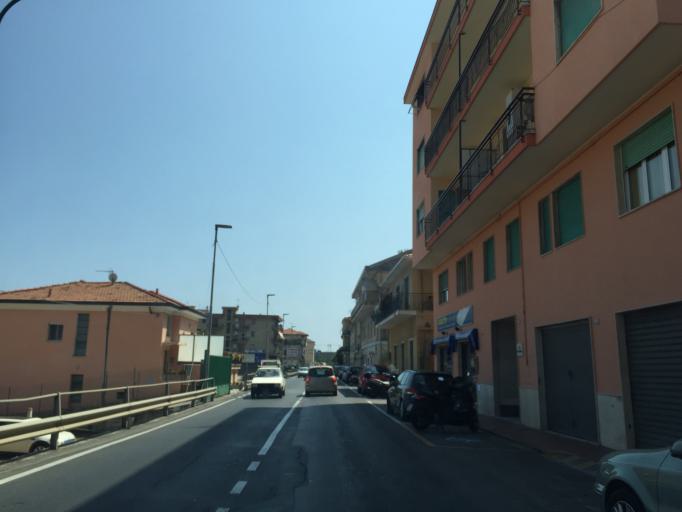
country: IT
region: Liguria
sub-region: Provincia di Imperia
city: Vallecrosia
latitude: 43.7914
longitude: 7.6292
